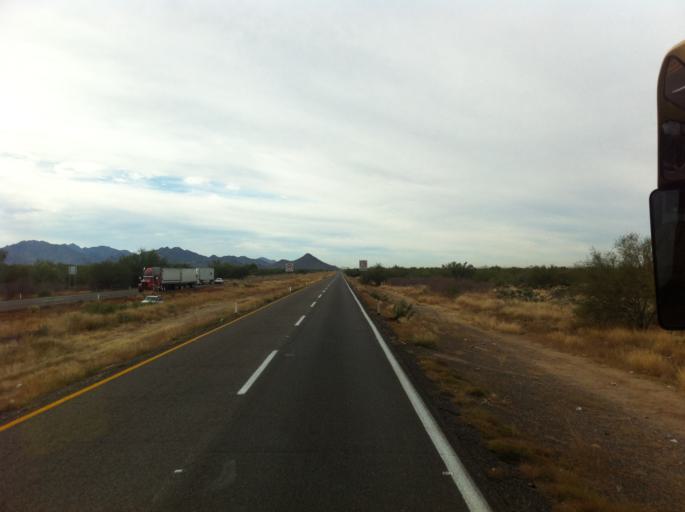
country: MX
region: Sonora
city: Hermosillo
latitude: 28.7080
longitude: -110.9852
